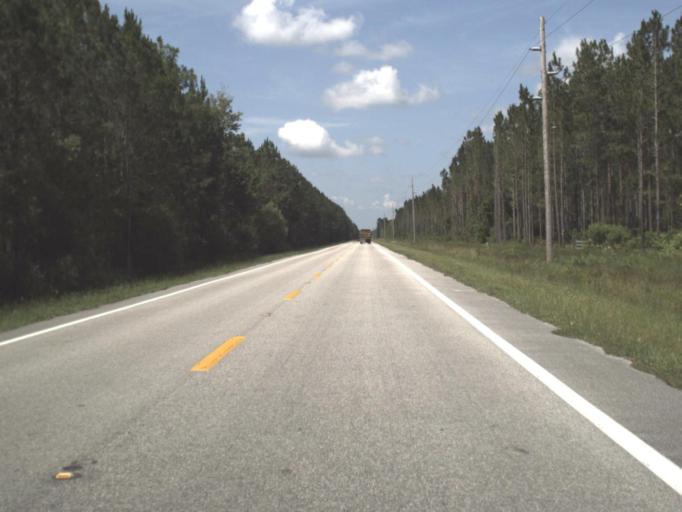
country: US
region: Florida
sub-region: Levy County
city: Bronson
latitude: 29.3783
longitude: -82.7135
